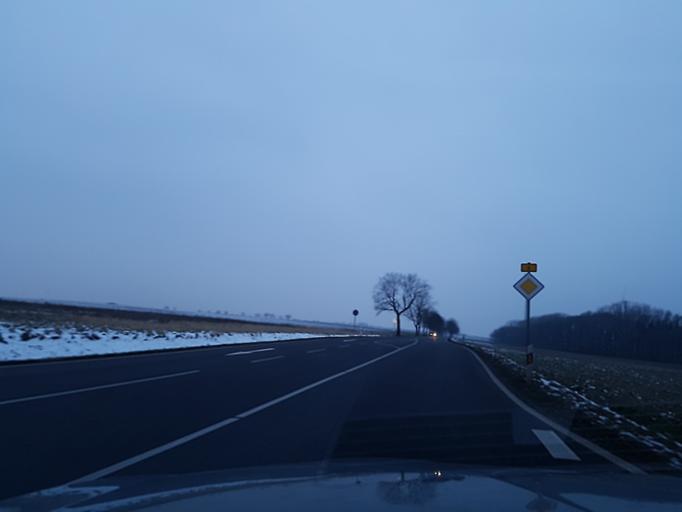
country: DE
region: Saxony
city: Stauchitz
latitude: 51.2712
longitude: 13.2351
